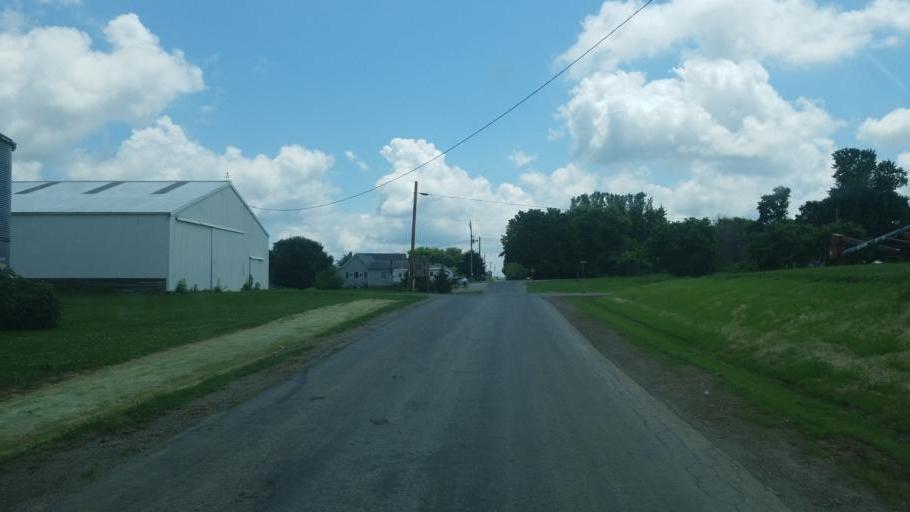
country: US
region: Ohio
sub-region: Highland County
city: Greenfield
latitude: 39.2637
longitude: -83.4456
